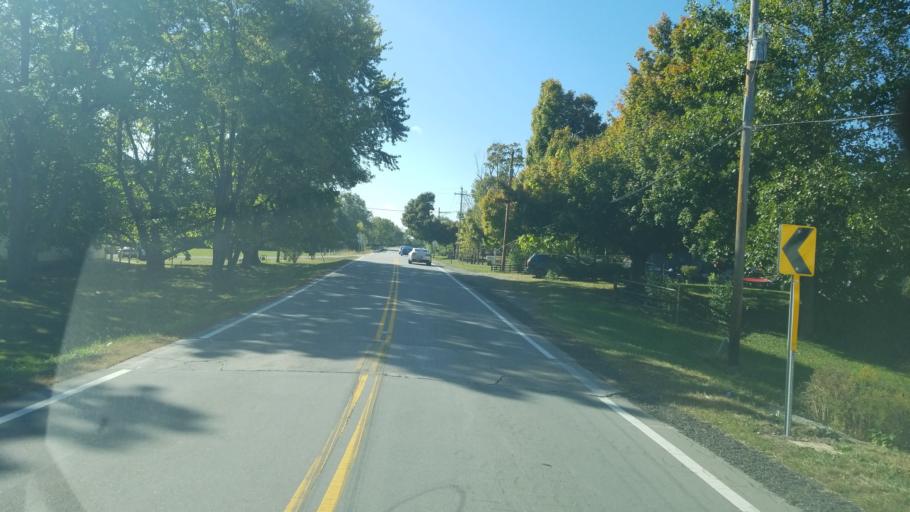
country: US
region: Ohio
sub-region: Fayette County
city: Washington Court House
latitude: 39.4749
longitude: -83.4838
